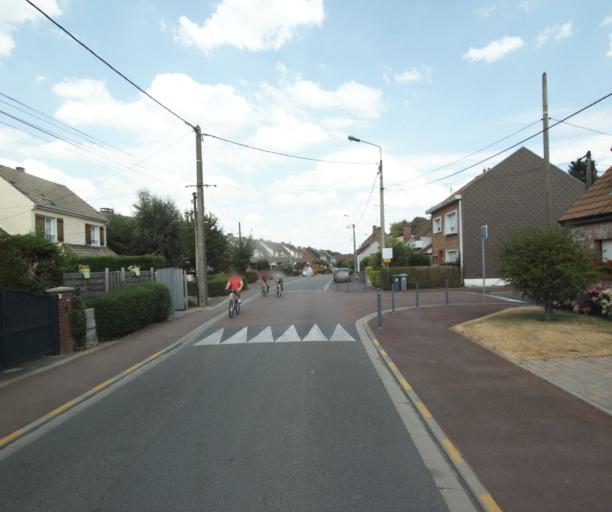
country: FR
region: Nord-Pas-de-Calais
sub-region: Departement du Nord
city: Neuville-en-Ferrain
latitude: 50.7463
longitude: 3.1600
